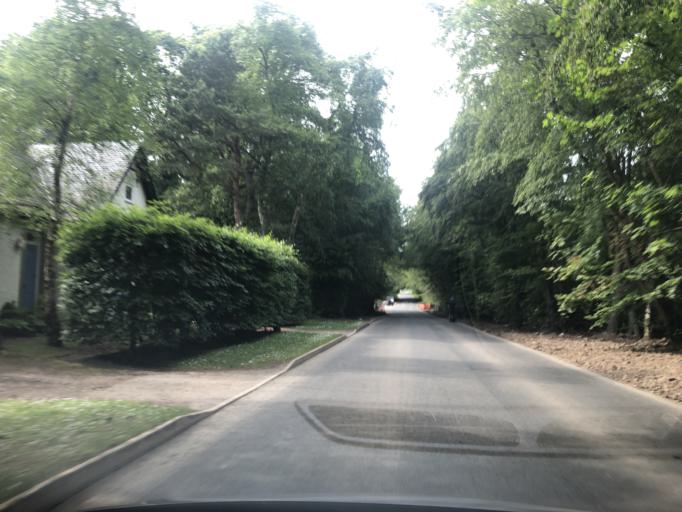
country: GB
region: Scotland
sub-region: Midlothian
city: Penicuik
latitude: 55.8451
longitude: -3.2257
